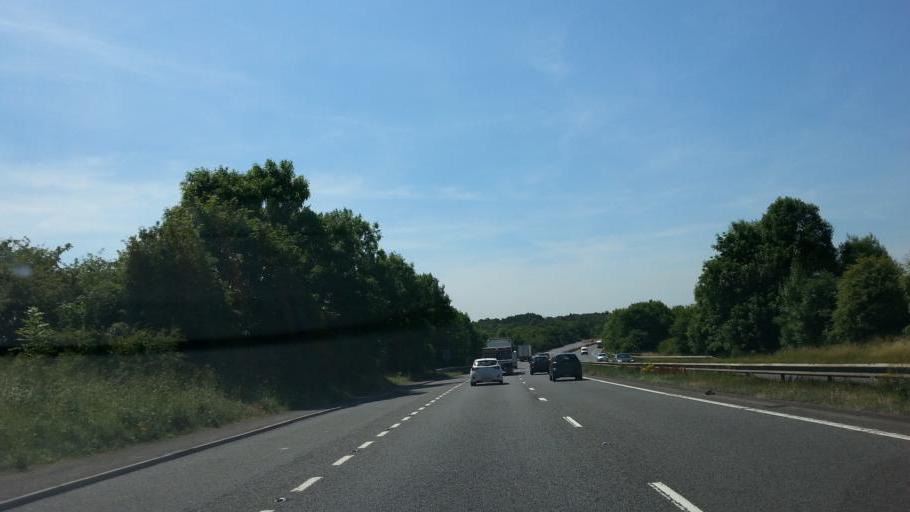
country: GB
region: England
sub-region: Derbyshire
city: Ripley
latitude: 53.0642
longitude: -1.4103
